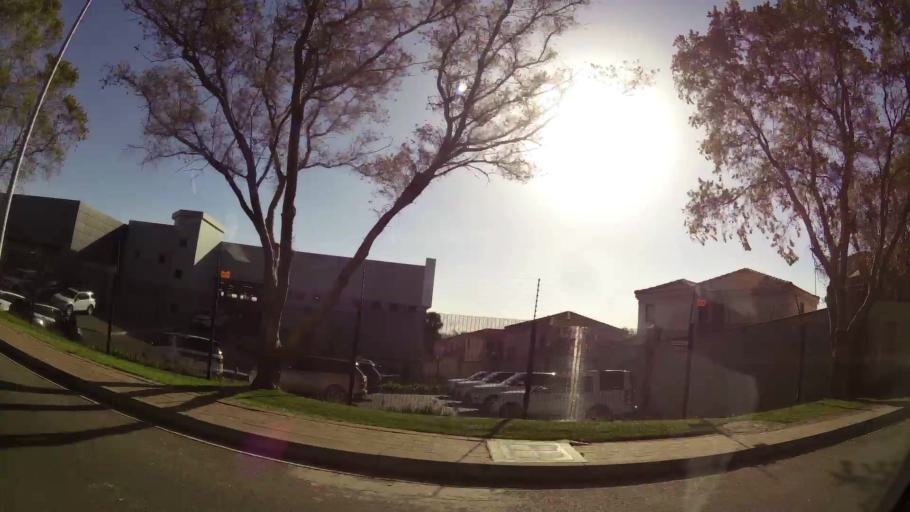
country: ZA
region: Gauteng
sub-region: City of Johannesburg Metropolitan Municipality
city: Diepsloot
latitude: -26.0252
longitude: 27.9842
